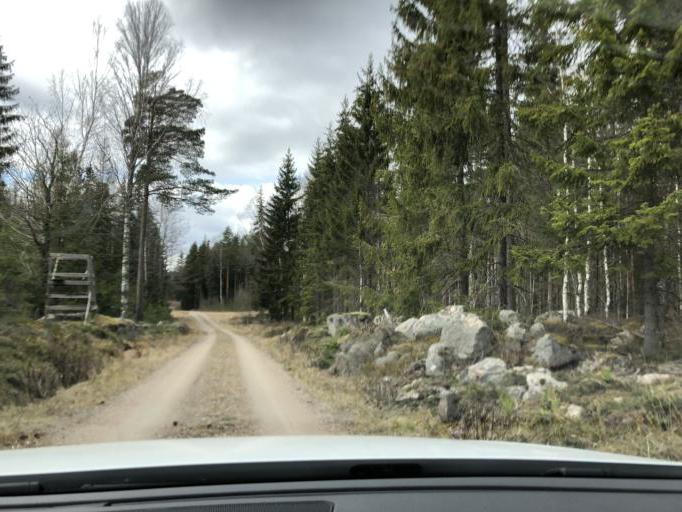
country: SE
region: Gaevleborg
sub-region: Gavle Kommun
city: Hedesunda
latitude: 60.3421
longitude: 17.0794
